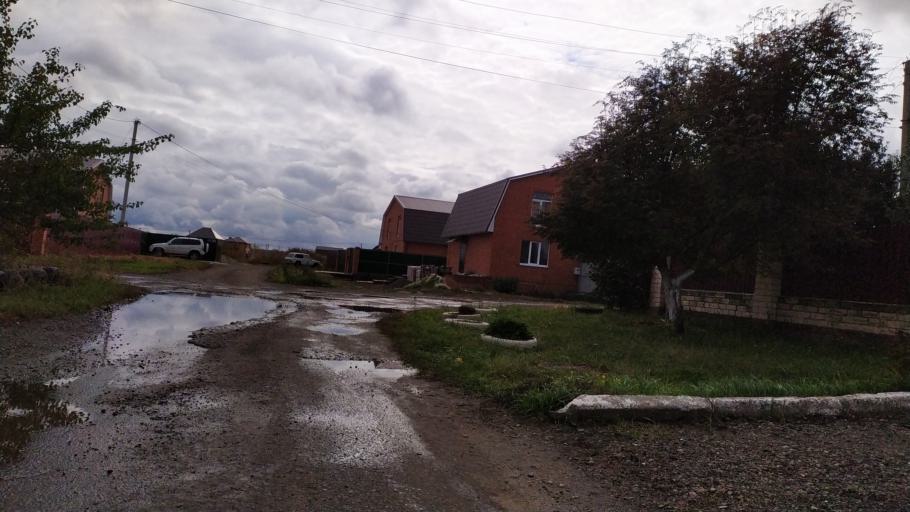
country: RU
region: Kursk
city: Kursk
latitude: 51.6426
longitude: 36.1558
